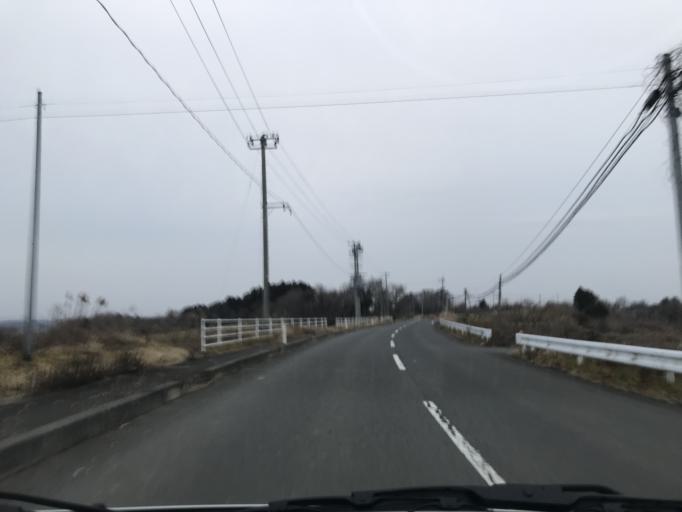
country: JP
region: Miyagi
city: Kogota
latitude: 38.6952
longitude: 141.0951
